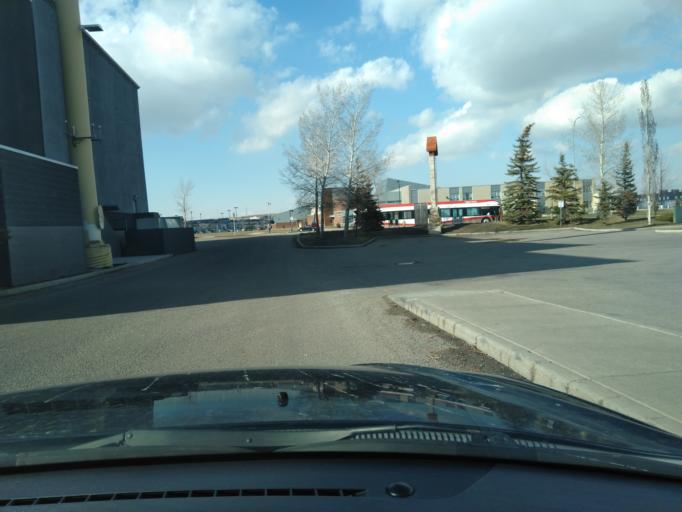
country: CA
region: Alberta
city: Calgary
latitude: 51.1557
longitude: -114.0665
